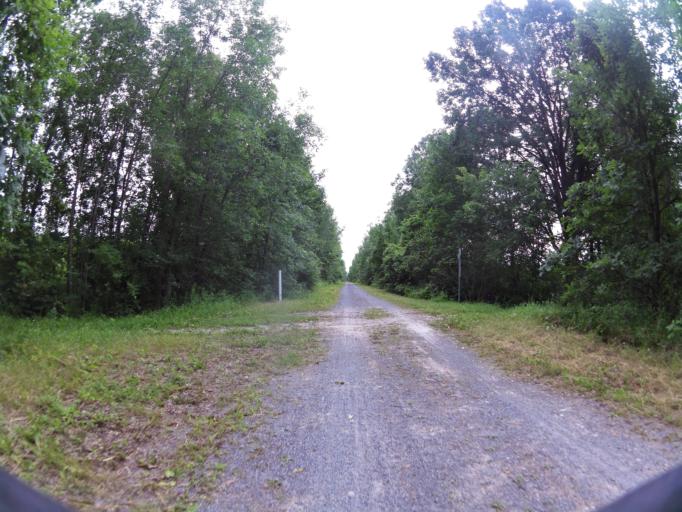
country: CA
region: Ontario
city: Ottawa
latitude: 45.1872
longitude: -75.6207
